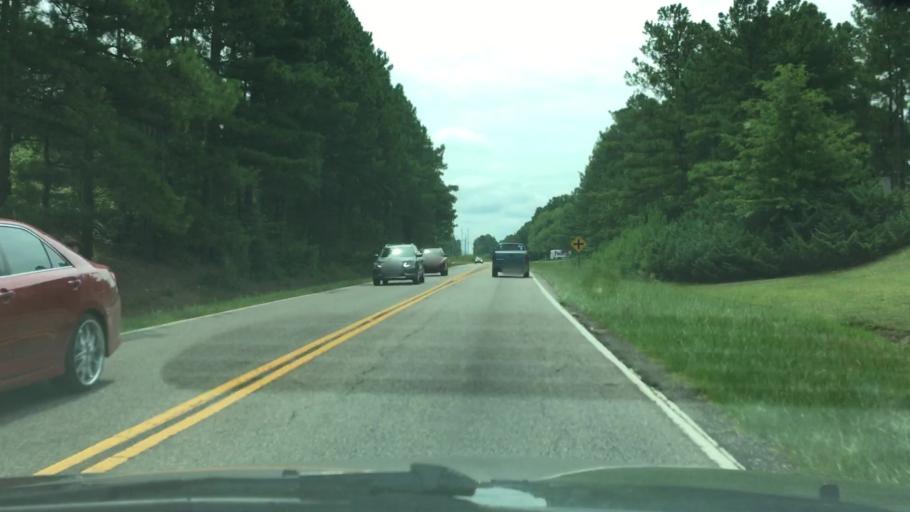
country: US
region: South Carolina
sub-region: Aiken County
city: Aiken
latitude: 33.5257
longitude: -81.7364
